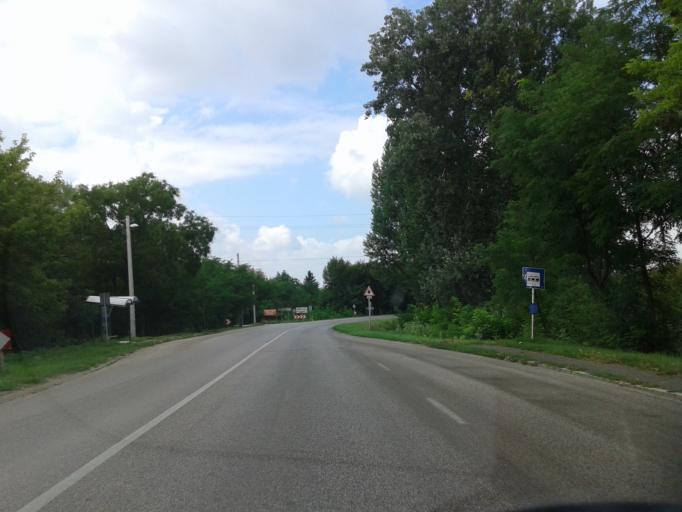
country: HU
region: Csongrad
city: Domaszek
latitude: 46.2743
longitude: 20.0252
